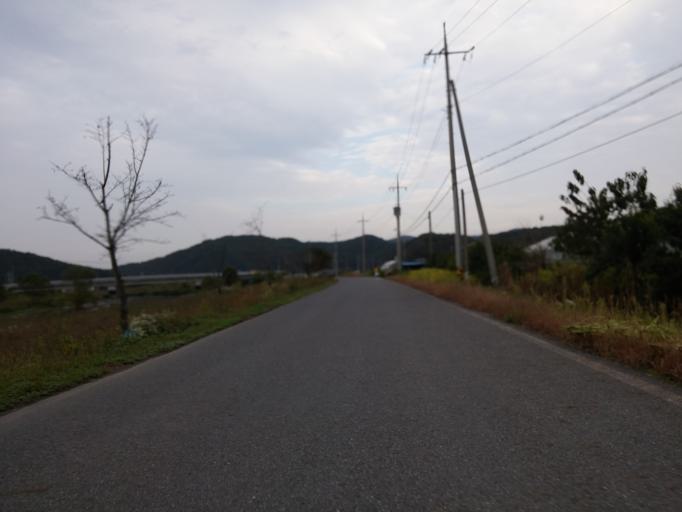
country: KR
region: Daejeon
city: Daejeon
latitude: 36.2459
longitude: 127.3144
